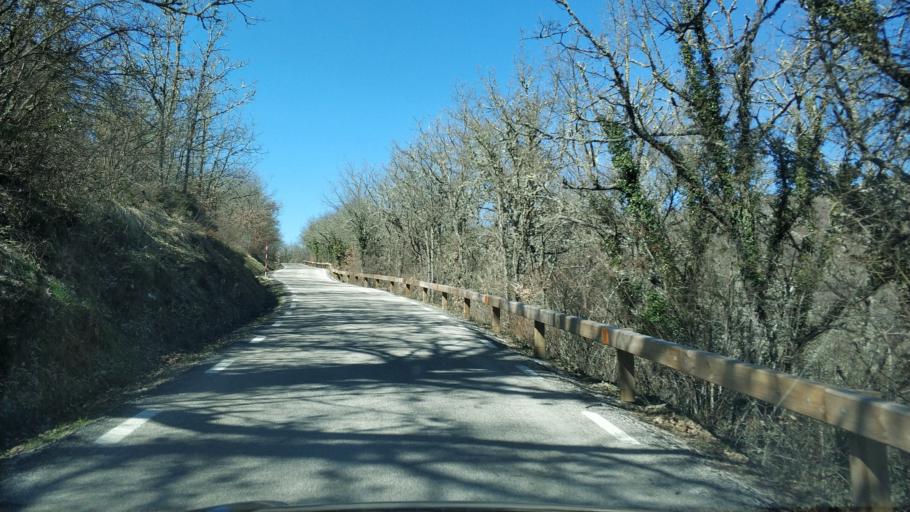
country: ES
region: Castille and Leon
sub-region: Provincia de Palencia
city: Berzosilla
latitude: 42.8692
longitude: -4.0633
